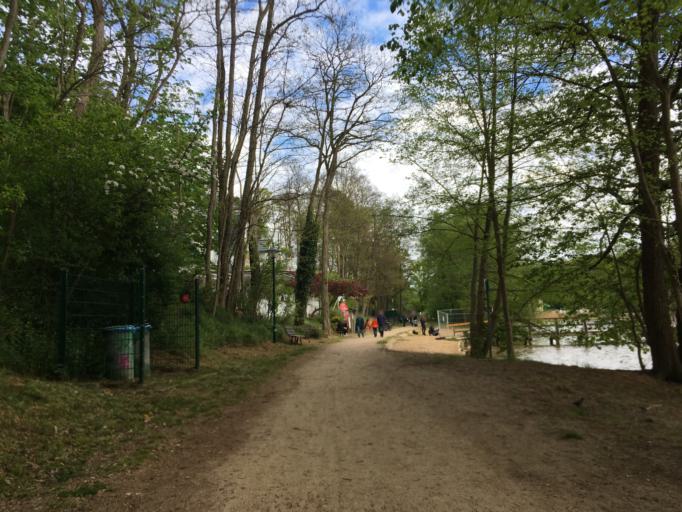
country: DE
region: Brandenburg
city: Rudnitz
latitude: 52.7611
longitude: 13.5561
